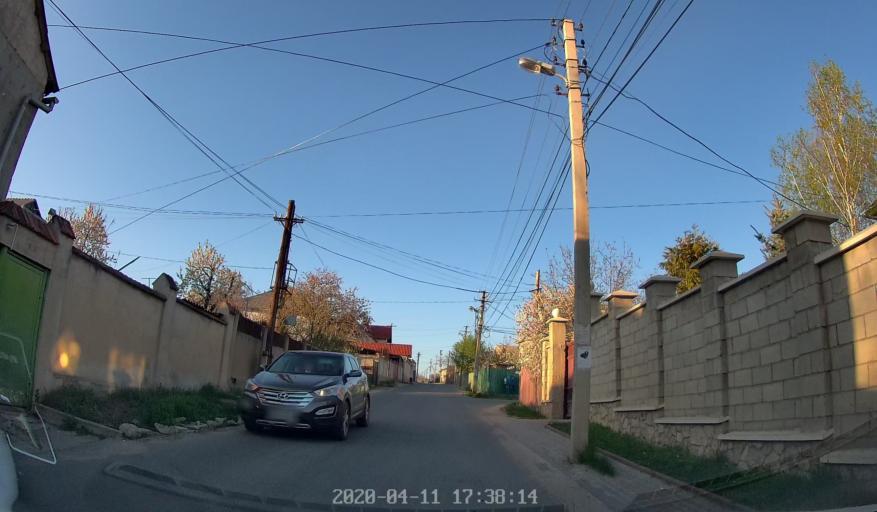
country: MD
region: Laloveni
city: Ialoveni
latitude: 46.9818
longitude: 28.8029
